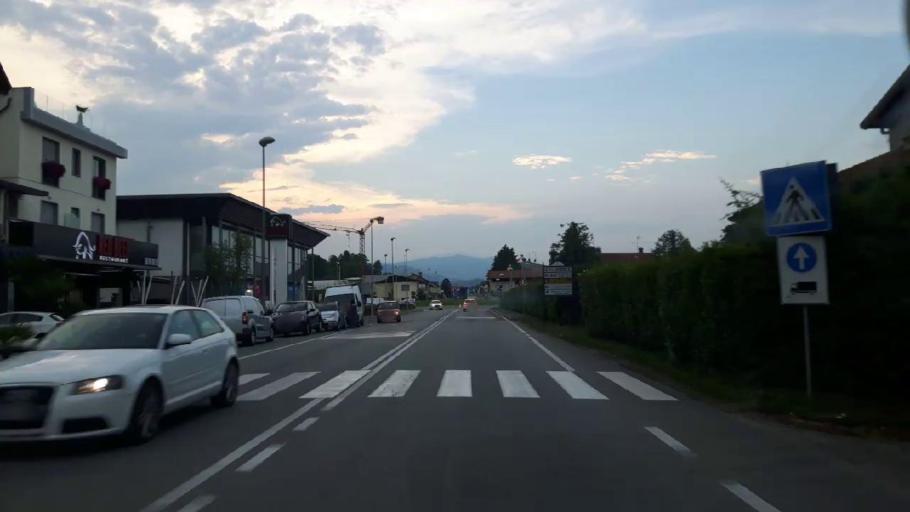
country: IT
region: Piedmont
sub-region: Provincia di Novara
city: Dormelletto
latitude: 45.7295
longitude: 8.5779
